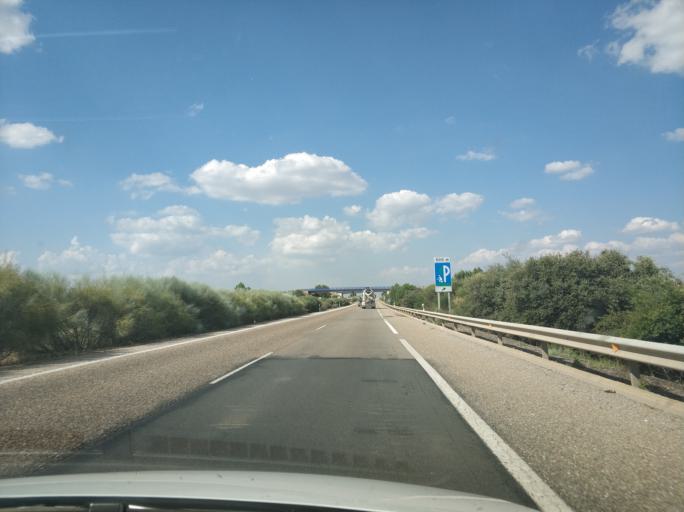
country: ES
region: Castille and Leon
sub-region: Provincia de Zamora
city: Matilla de Arzon
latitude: 42.1180
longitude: -5.6556
